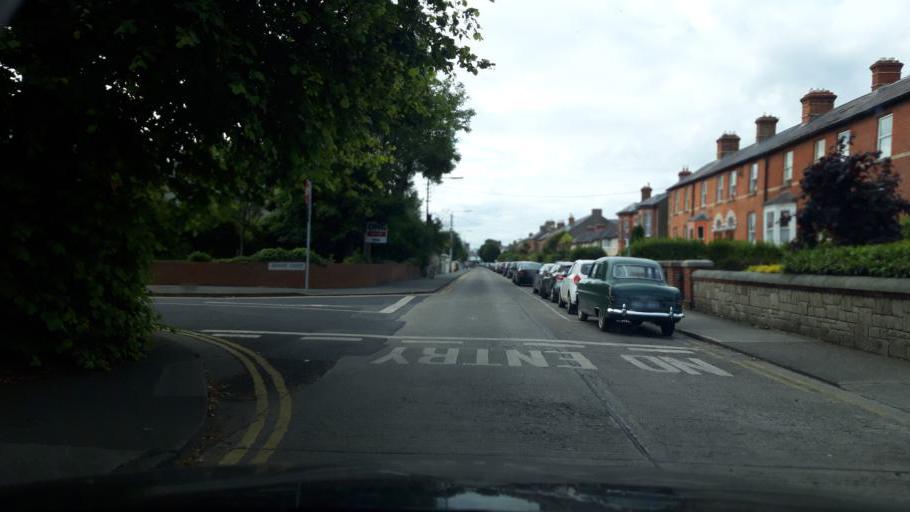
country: IE
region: Leinster
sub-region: Wicklow
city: Bray
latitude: 53.1998
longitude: -6.0990
